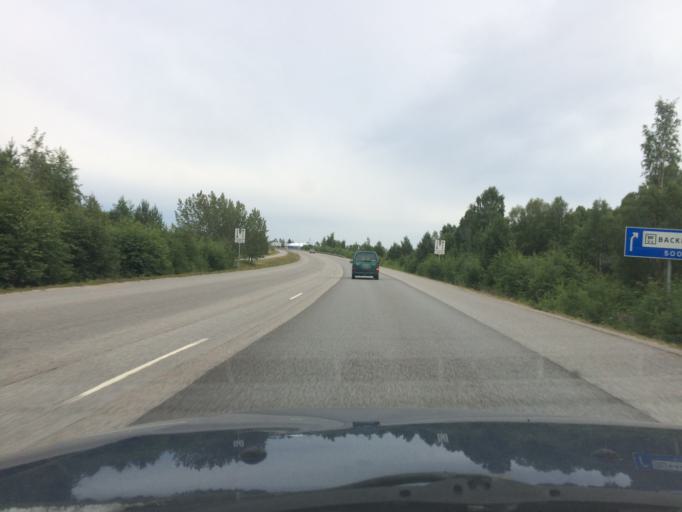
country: SE
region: Norrbotten
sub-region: Pitea Kommun
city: Pitea
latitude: 65.3273
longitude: 21.4307
